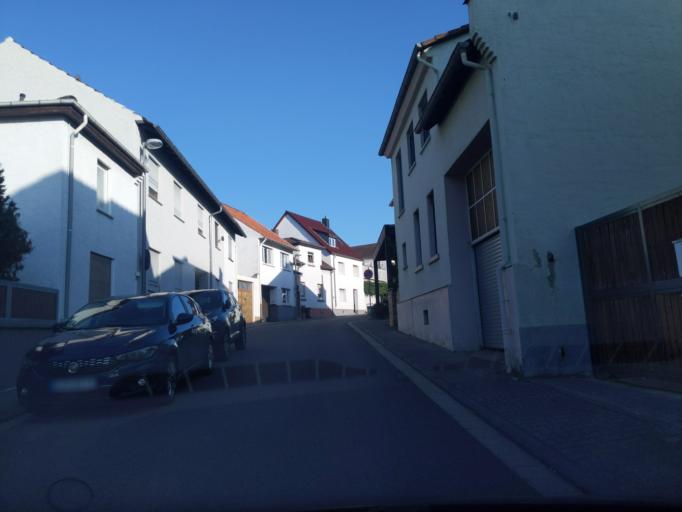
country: DE
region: Rheinland-Pfalz
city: Nieder-Ingelheim
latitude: 49.9814
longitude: 8.0716
